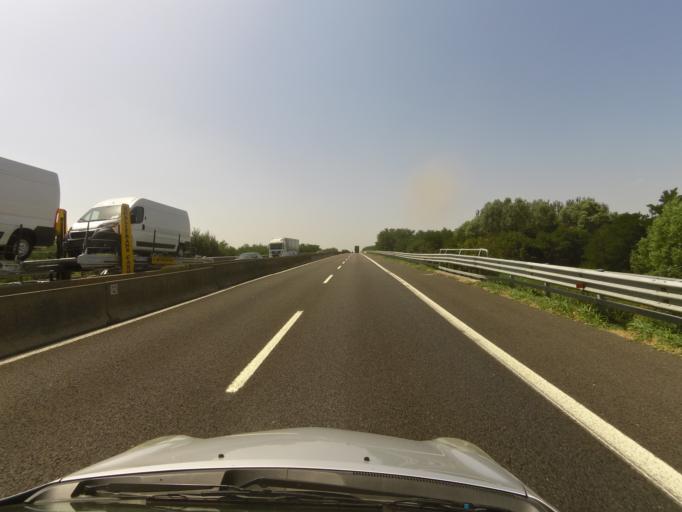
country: IT
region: Veneto
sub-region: Provincia di Rovigo
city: Villamarzana
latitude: 45.0081
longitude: 11.6812
